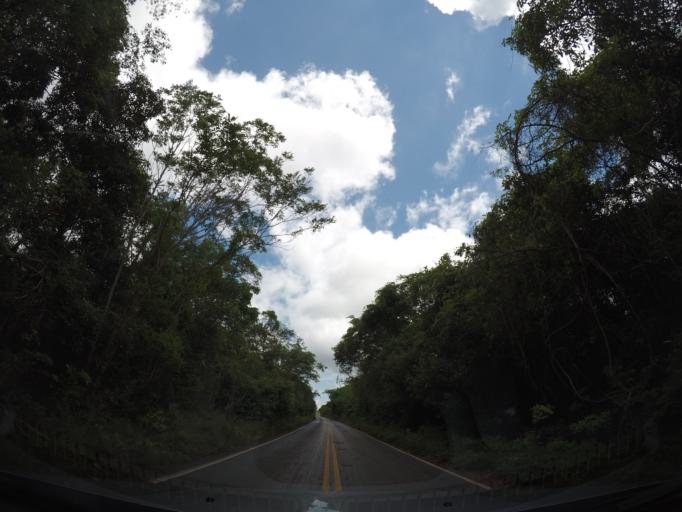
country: BR
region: Bahia
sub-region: Andarai
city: Vera Cruz
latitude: -12.5271
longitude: -41.3635
